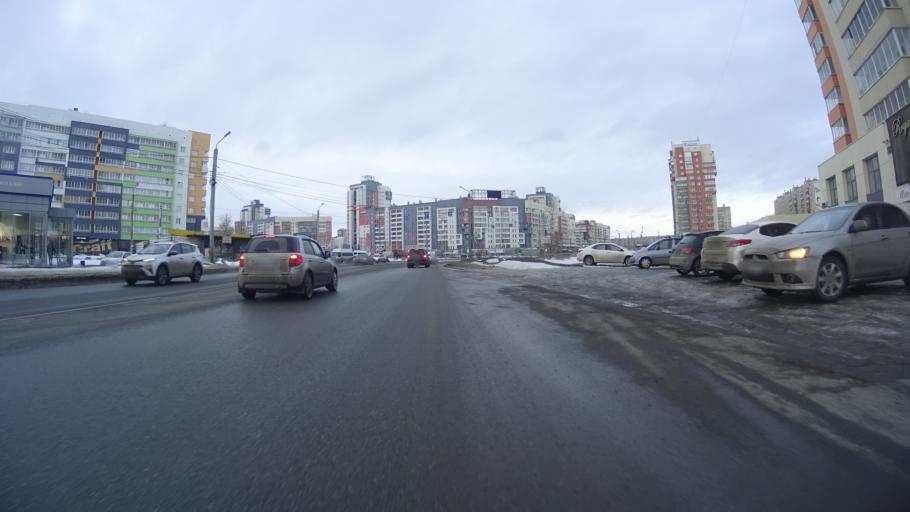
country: RU
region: Chelyabinsk
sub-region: Gorod Chelyabinsk
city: Chelyabinsk
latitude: 55.1624
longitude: 61.2956
